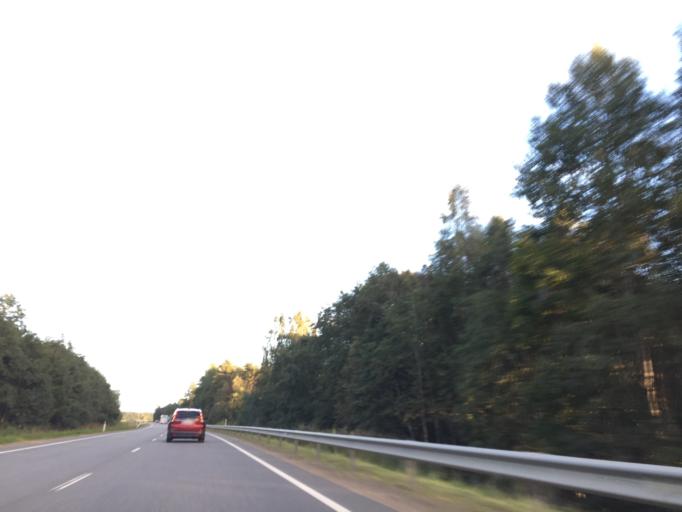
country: LV
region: Broceni
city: Broceni
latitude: 56.6690
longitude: 22.5909
